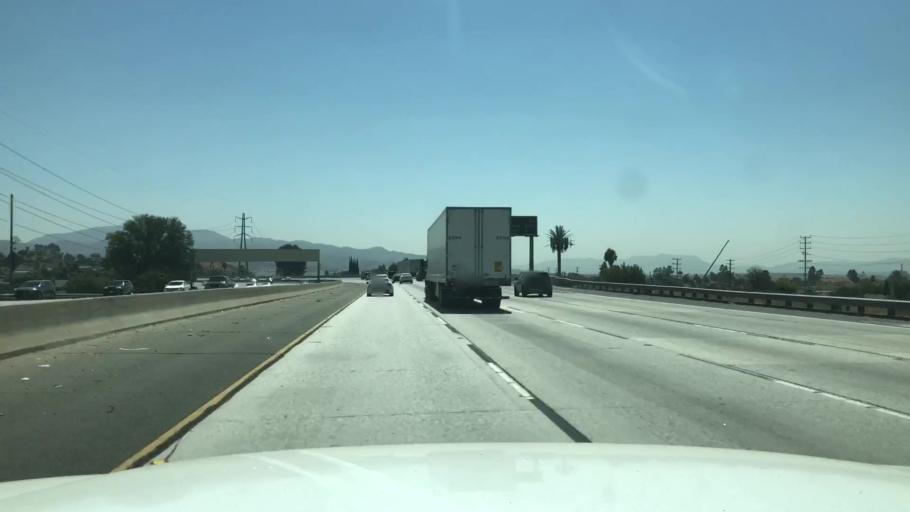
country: US
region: California
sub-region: Los Angeles County
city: San Fernando
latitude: 34.2801
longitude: -118.3992
